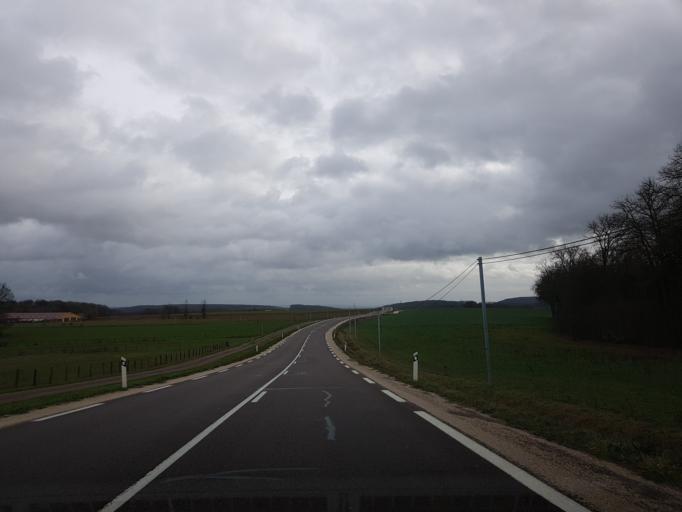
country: FR
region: Champagne-Ardenne
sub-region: Departement de la Haute-Marne
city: Fayl-Billot
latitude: 47.7681
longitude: 5.7071
